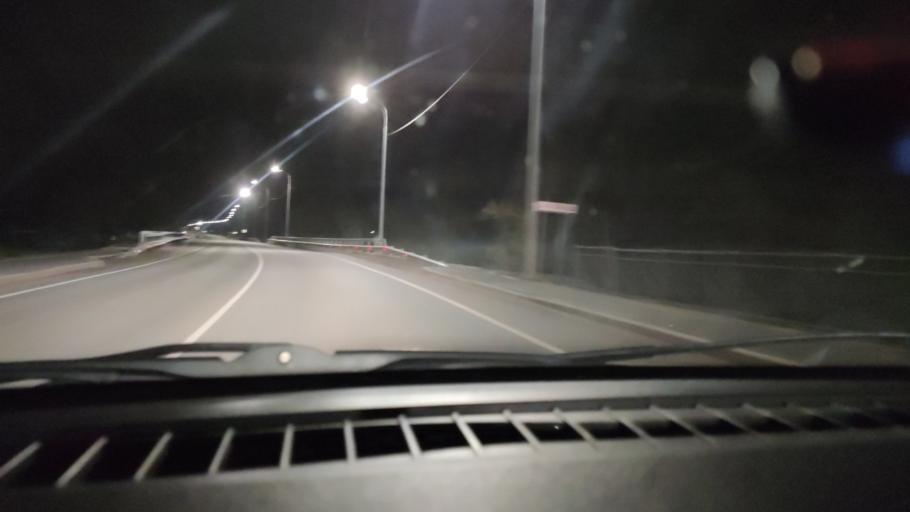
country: RU
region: Bashkortostan
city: Yermolayevo
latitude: 52.5877
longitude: 55.8505
